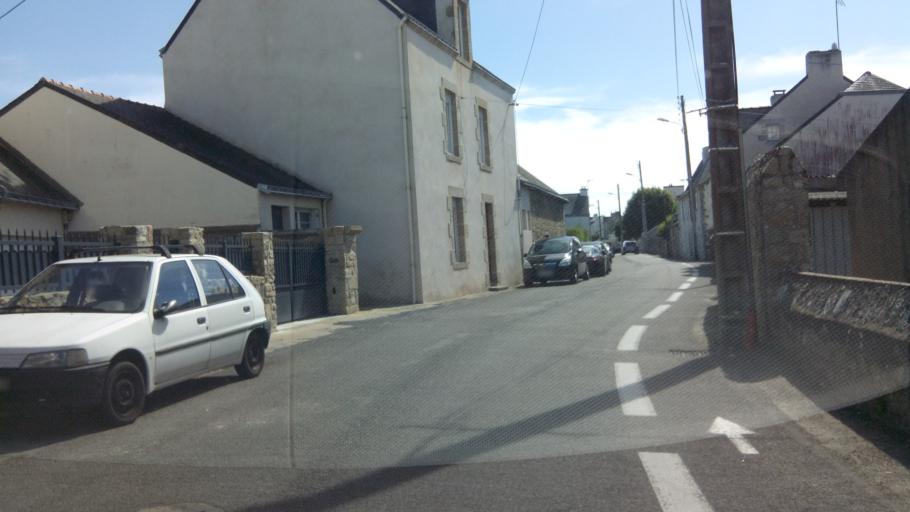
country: FR
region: Pays de la Loire
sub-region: Departement de la Loire-Atlantique
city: Le Croisic
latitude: 47.2943
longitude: -2.5153
